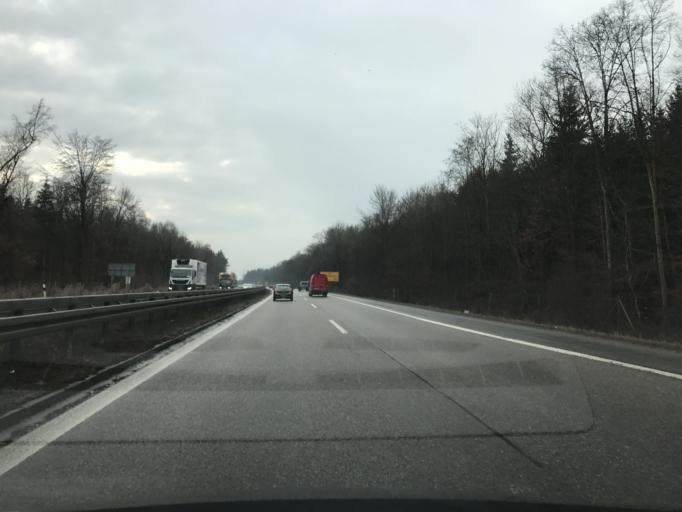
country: DE
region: Baden-Wuerttemberg
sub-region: Tuebingen Region
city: Ulm
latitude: 48.3560
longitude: 9.9609
